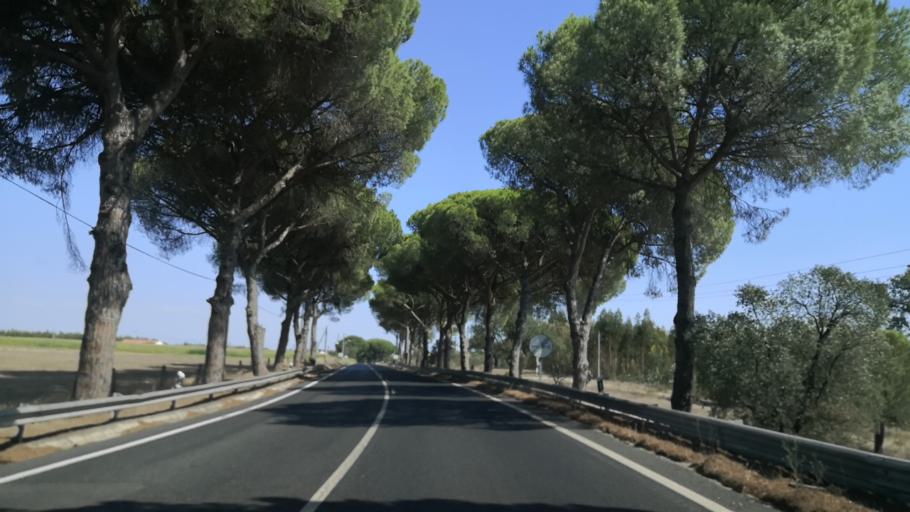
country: PT
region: Santarem
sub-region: Benavente
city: Poceirao
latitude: 38.7236
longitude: -8.6406
